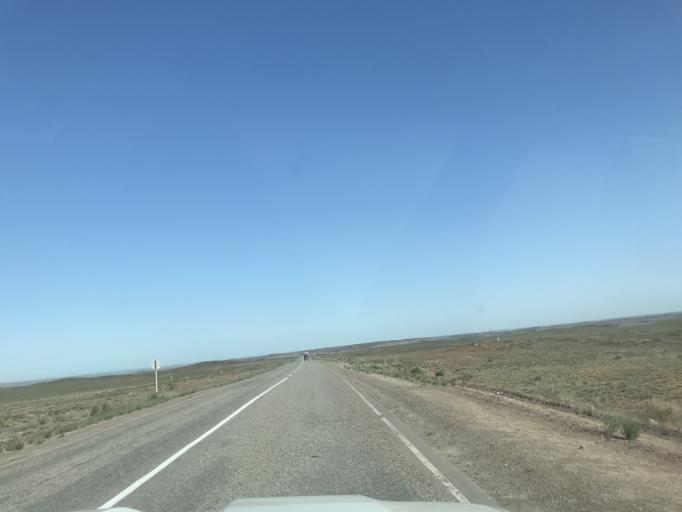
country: KZ
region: Zhambyl
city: Mynaral
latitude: 45.4696
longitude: 73.5596
